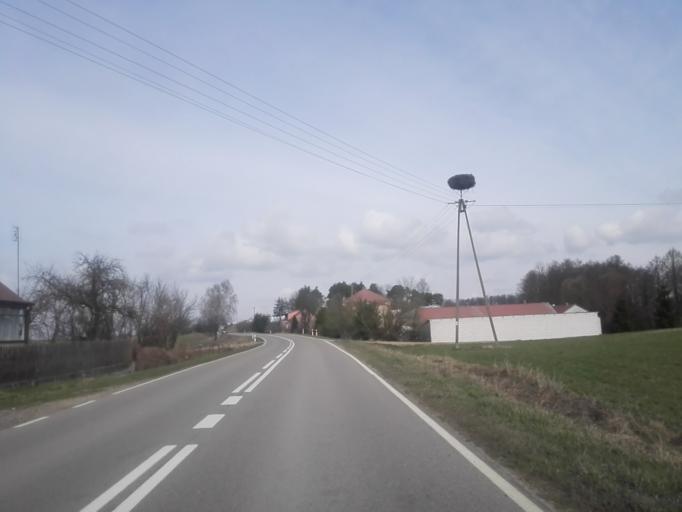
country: PL
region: Podlasie
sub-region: Powiat sejnenski
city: Sejny
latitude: 54.0800
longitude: 23.3488
